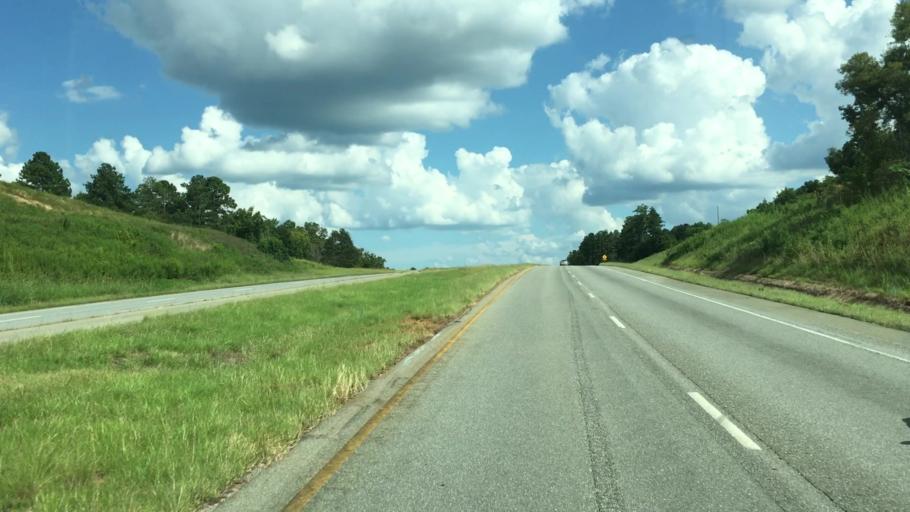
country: US
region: Georgia
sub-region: Wilkinson County
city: Irwinton
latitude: 32.7094
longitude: -83.1345
